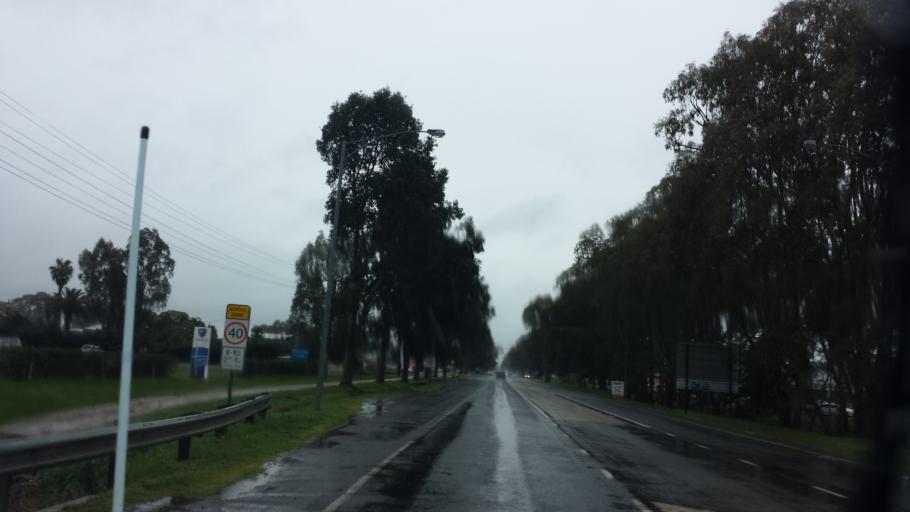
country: AU
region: Victoria
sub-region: Benalla
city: Benalla
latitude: -36.5482
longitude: 145.9981
